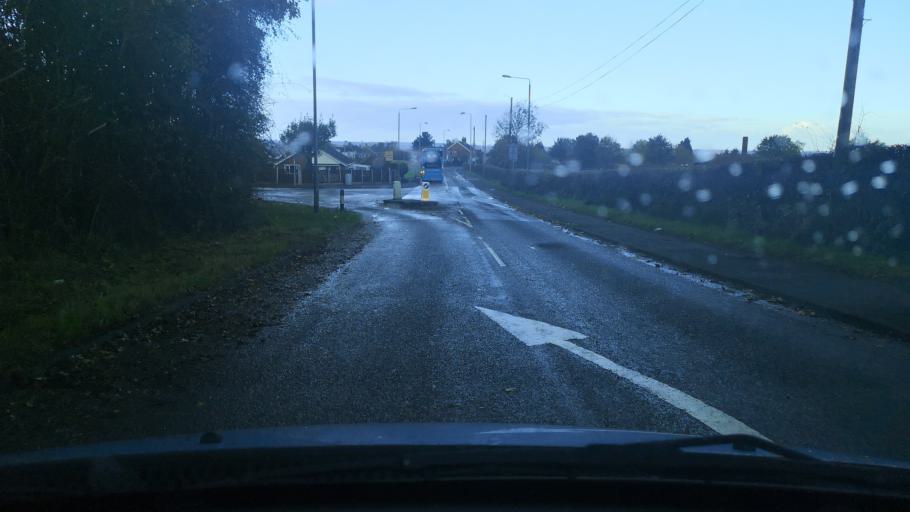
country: GB
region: England
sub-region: City and Borough of Wakefield
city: Crigglestone
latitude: 53.6278
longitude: -1.5244
